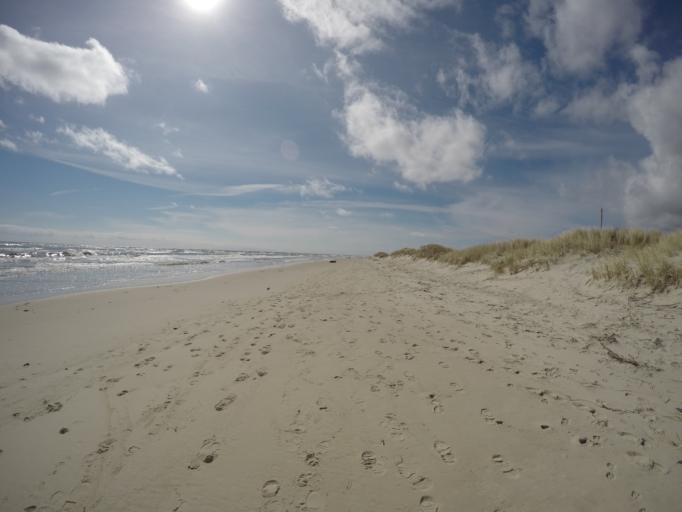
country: SE
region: Skane
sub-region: Simrishamns Kommun
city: Simrishamn
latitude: 55.3975
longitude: 14.2127
